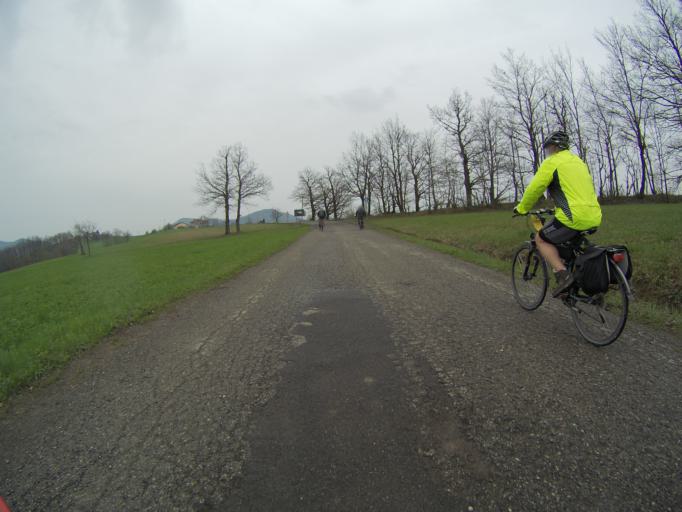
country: IT
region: Emilia-Romagna
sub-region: Provincia di Reggio Emilia
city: Ciano d'Enza
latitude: 44.5393
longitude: 10.4192
